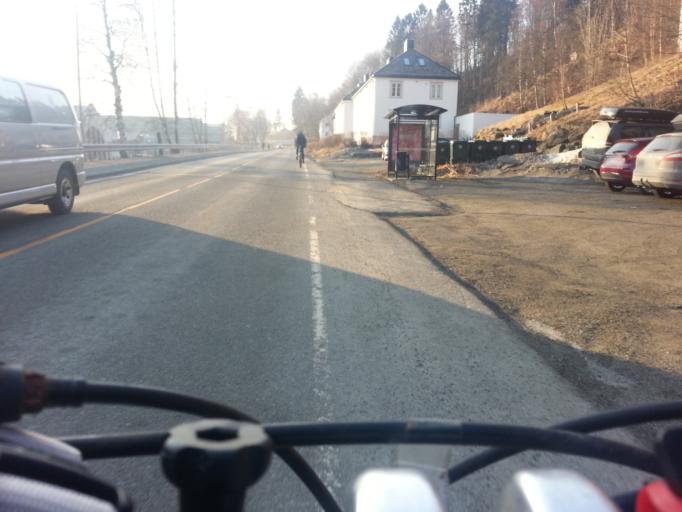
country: NO
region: Sor-Trondelag
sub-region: Trondheim
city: Trondheim
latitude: 63.4195
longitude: 10.3774
